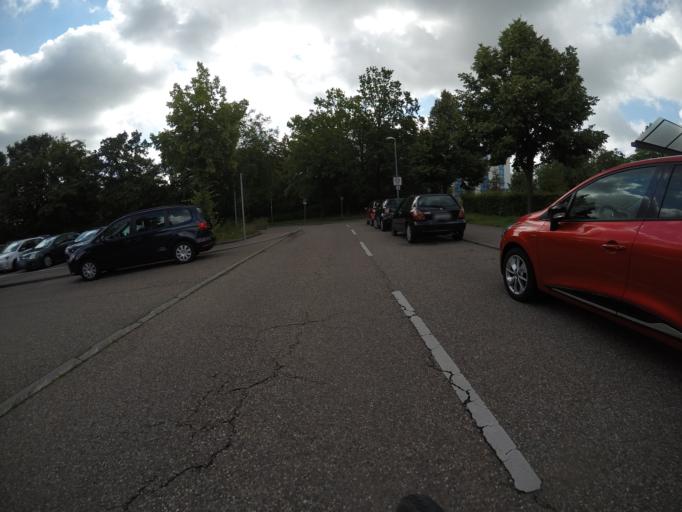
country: DE
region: Baden-Wuerttemberg
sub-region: Regierungsbezirk Stuttgart
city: Ostfildern
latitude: 48.7416
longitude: 9.2186
